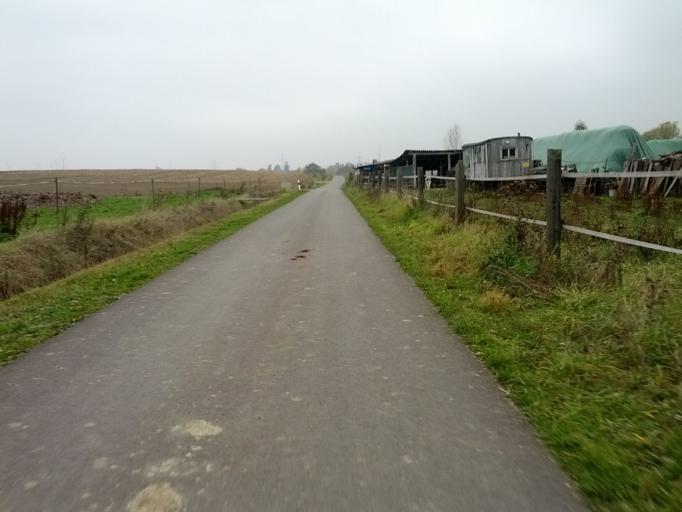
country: DE
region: Thuringia
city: Seebach
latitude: 50.9852
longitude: 10.4147
